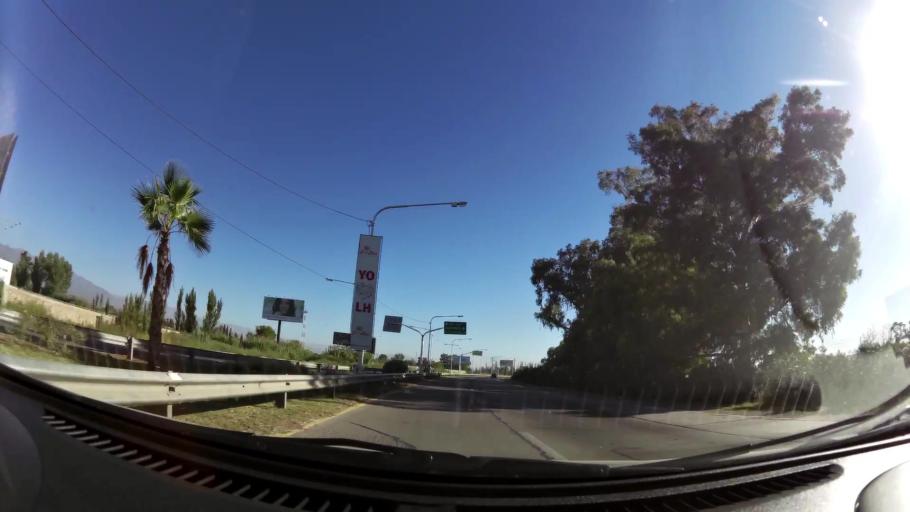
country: AR
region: Mendoza
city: Las Heras
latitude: -32.8327
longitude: -68.8068
